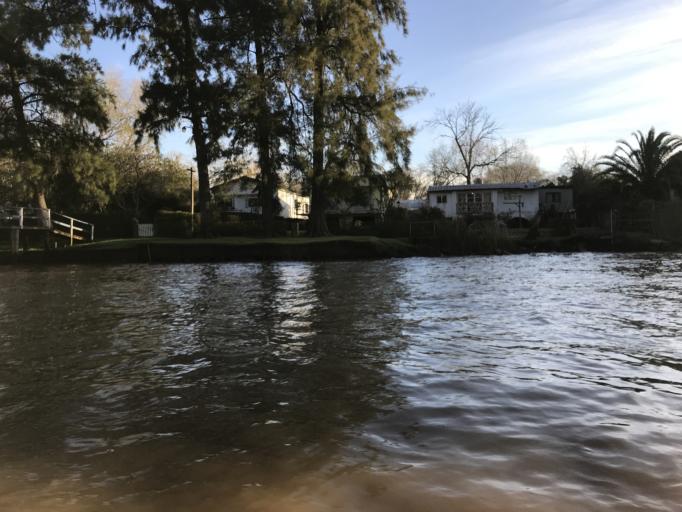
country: AR
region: Buenos Aires
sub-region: Partido de Tigre
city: Tigre
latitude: -34.3922
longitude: -58.5739
